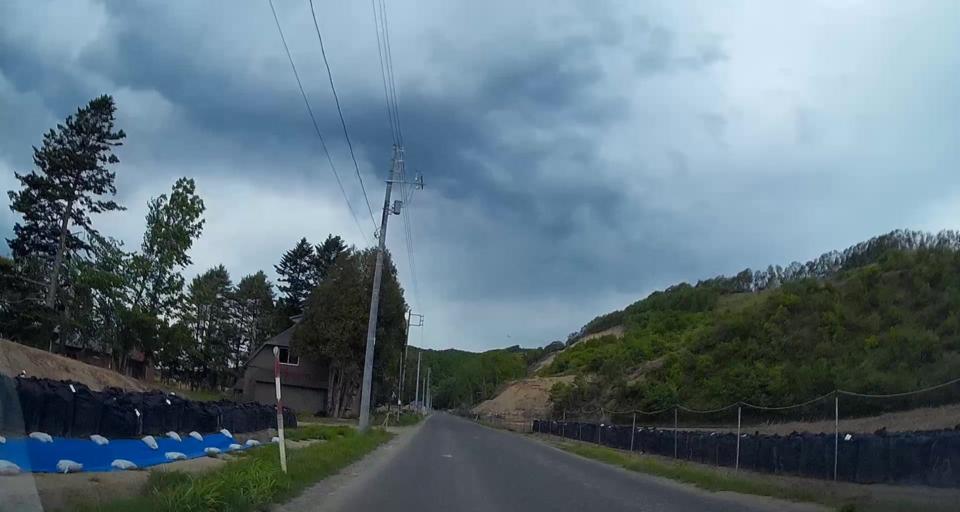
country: JP
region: Hokkaido
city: Chitose
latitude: 42.7580
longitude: 141.9668
